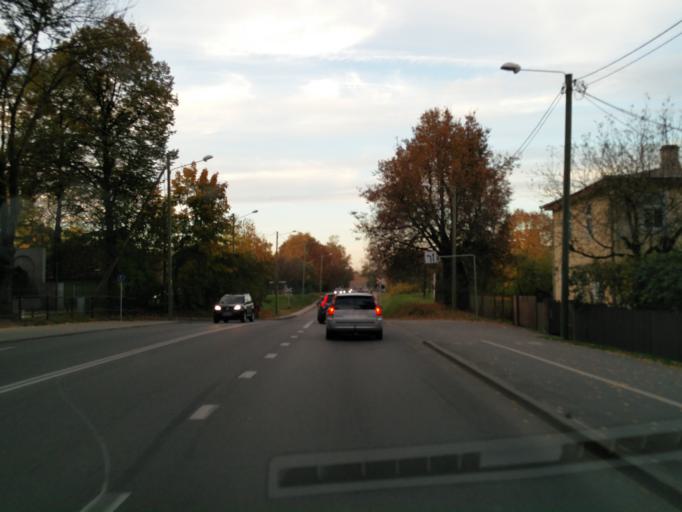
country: EE
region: Tartu
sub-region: Tartu linn
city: Tartu
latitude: 58.3593
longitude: 26.7215
